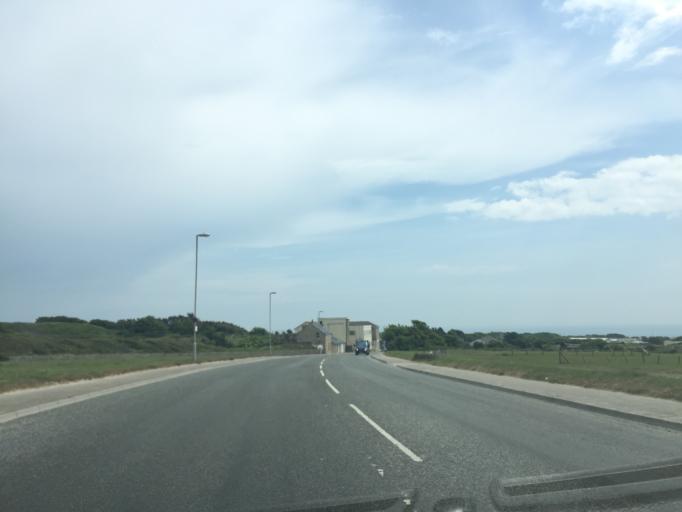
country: GB
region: England
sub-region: Dorset
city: Fortuneswell
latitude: 50.5543
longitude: -2.4398
